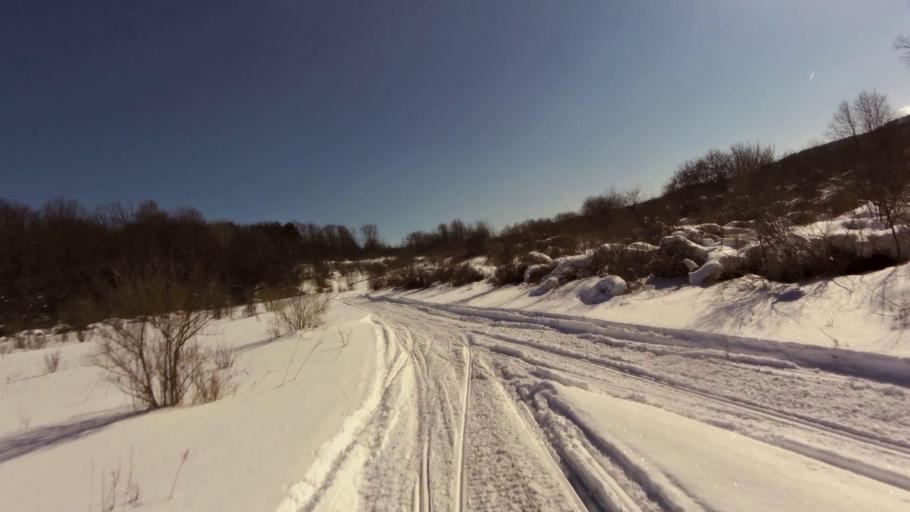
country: US
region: New York
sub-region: Cattaraugus County
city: Franklinville
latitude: 42.3468
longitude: -78.4369
